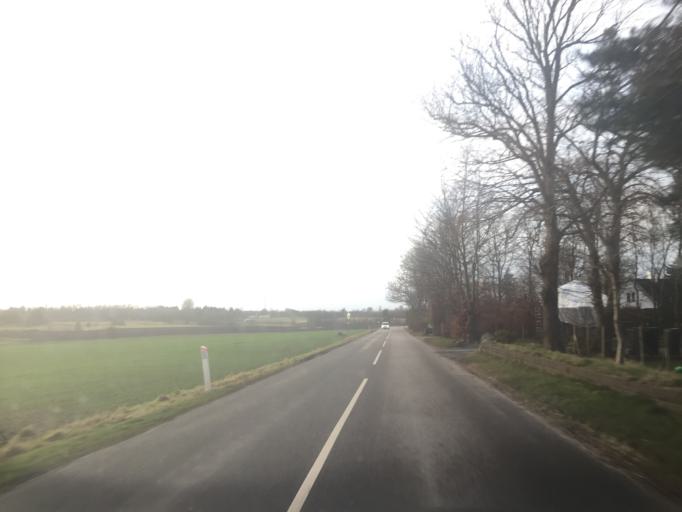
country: DK
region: Capital Region
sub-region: Egedal Kommune
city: Smorumnedre
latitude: 55.7139
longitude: 12.2830
